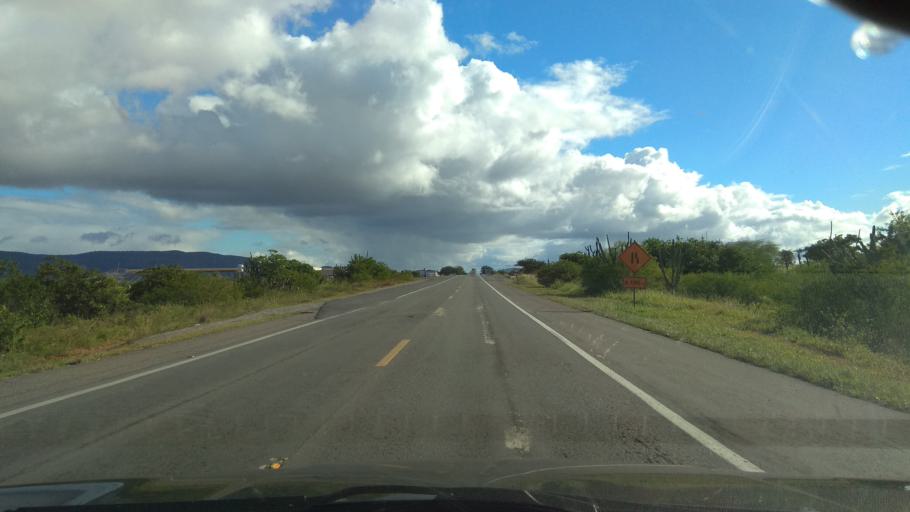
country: BR
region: Bahia
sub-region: Castro Alves
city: Castro Alves
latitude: -12.6814
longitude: -39.6726
